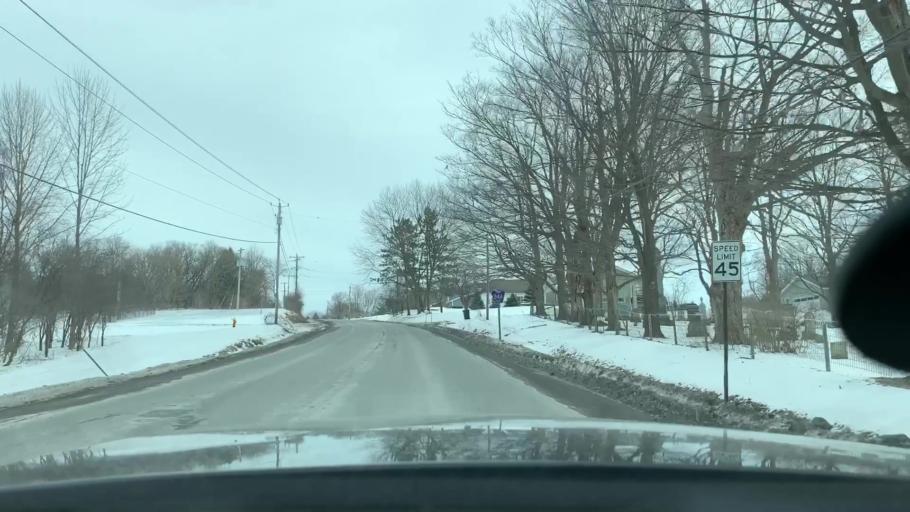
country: US
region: New York
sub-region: Oneida County
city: Washington Mills
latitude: 43.0518
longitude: -75.2406
